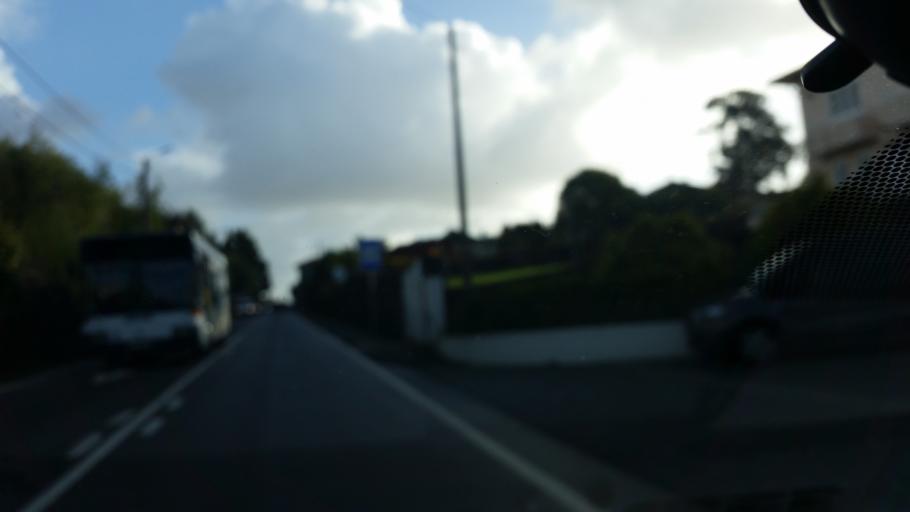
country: PT
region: Porto
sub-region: Santo Tirso
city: Sao Miguel do Couto
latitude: 41.3576
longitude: -8.4445
